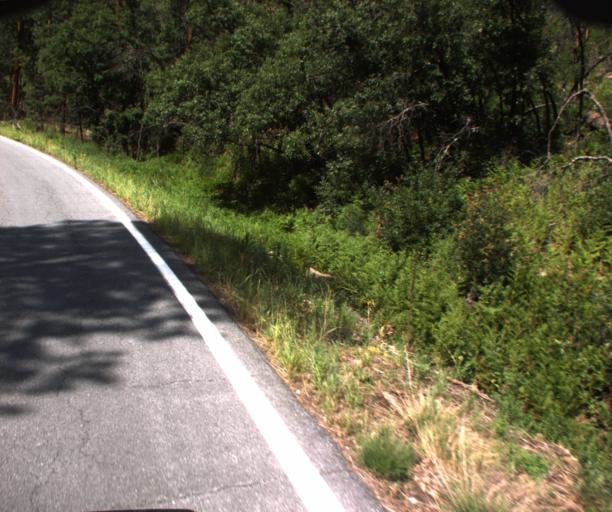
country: US
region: Arizona
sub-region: Apache County
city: Eagar
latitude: 33.7767
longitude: -109.1852
